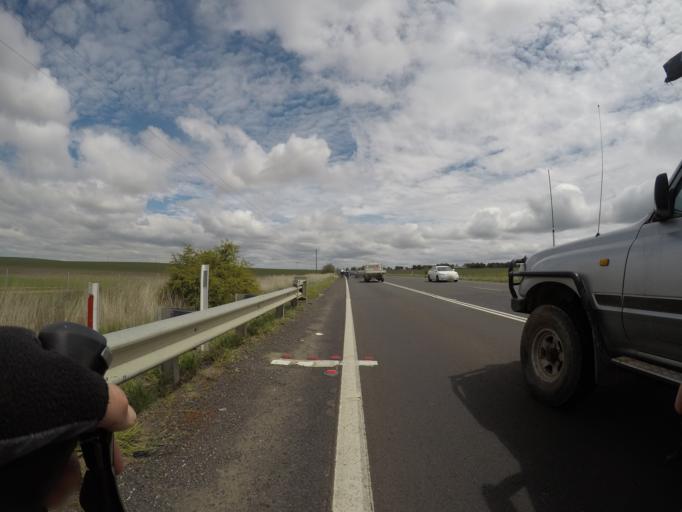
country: AU
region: New South Wales
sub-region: Bathurst Regional
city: Kelso
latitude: -33.4243
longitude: 149.6655
